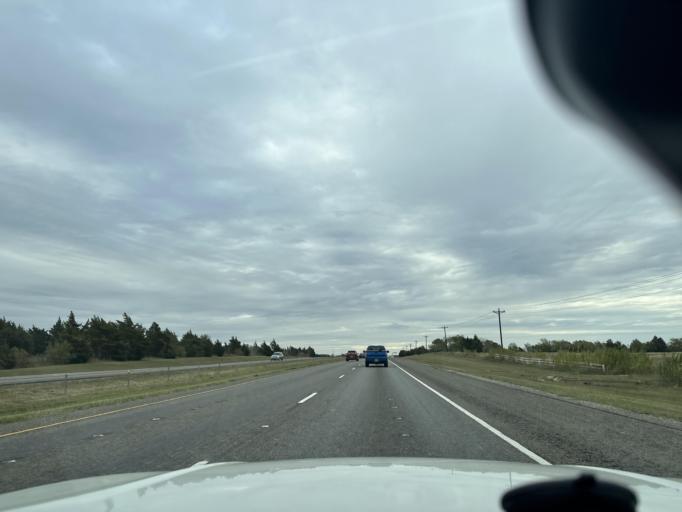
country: US
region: Texas
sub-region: Washington County
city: Brenham
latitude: 30.1904
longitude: -96.5391
